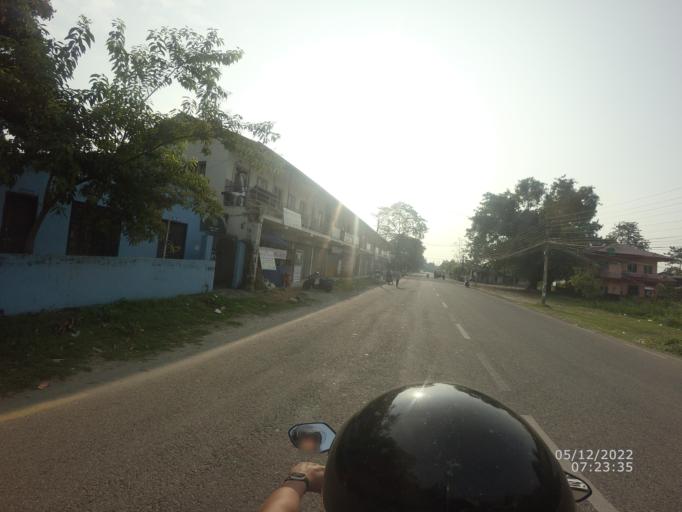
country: NP
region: Central Region
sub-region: Narayani Zone
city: Bharatpur
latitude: 27.6804
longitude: 84.4358
